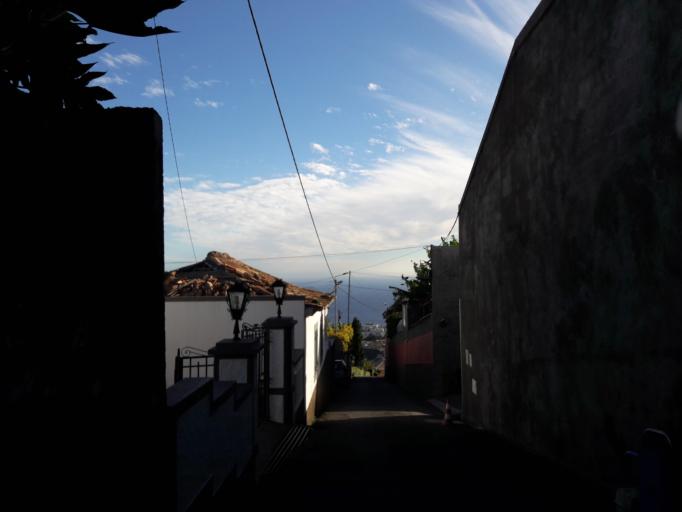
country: PT
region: Madeira
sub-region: Funchal
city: Nossa Senhora do Monte
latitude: 32.6692
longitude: -16.9216
